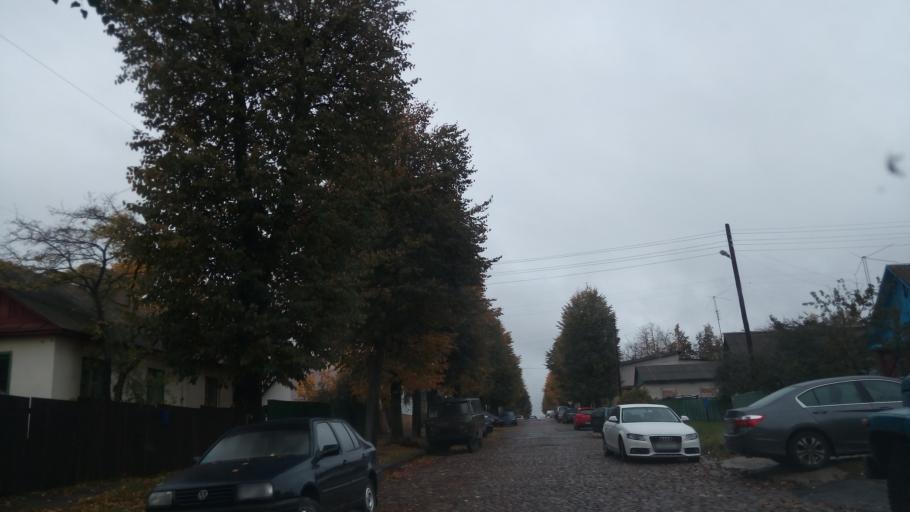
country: BY
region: Minsk
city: Minsk
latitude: 53.9441
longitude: 27.5962
